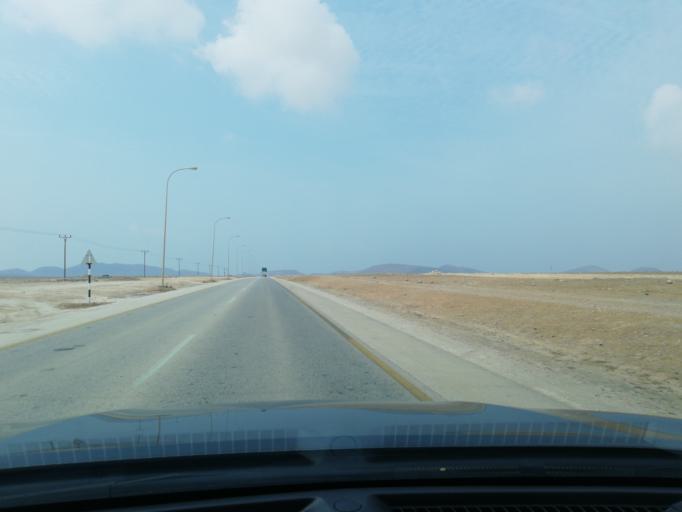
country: OM
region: Zufar
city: Salalah
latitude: 16.9341
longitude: 53.8434
